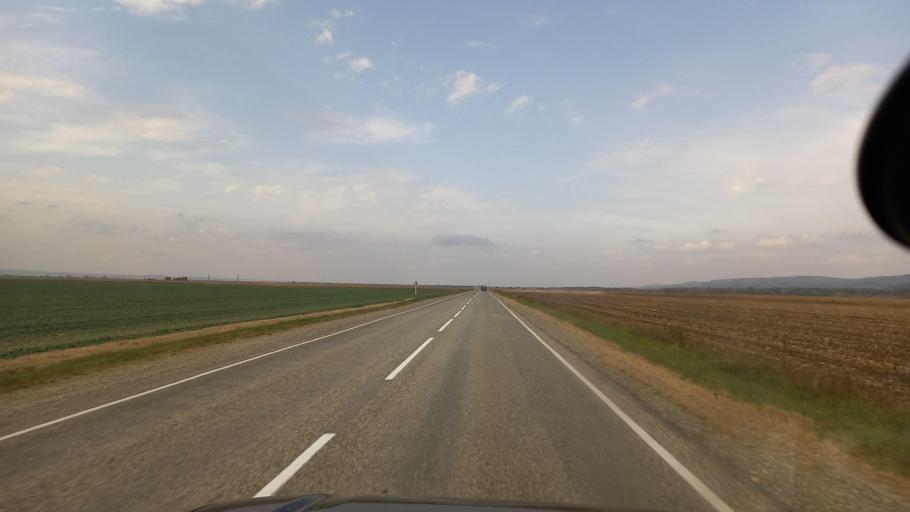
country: RU
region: Krasnodarskiy
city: Perepravnaya
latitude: 44.3109
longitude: 40.8572
